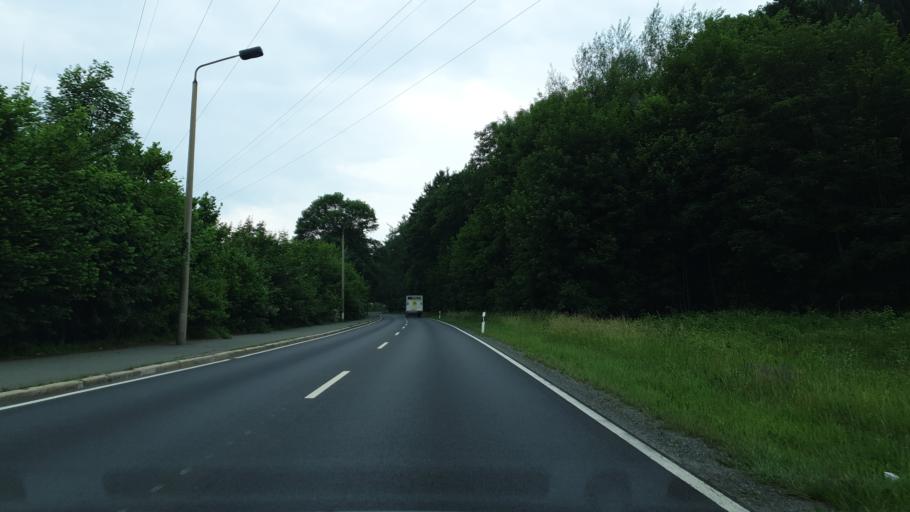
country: DE
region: Saxony
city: Auerbach
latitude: 50.5199
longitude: 12.4011
